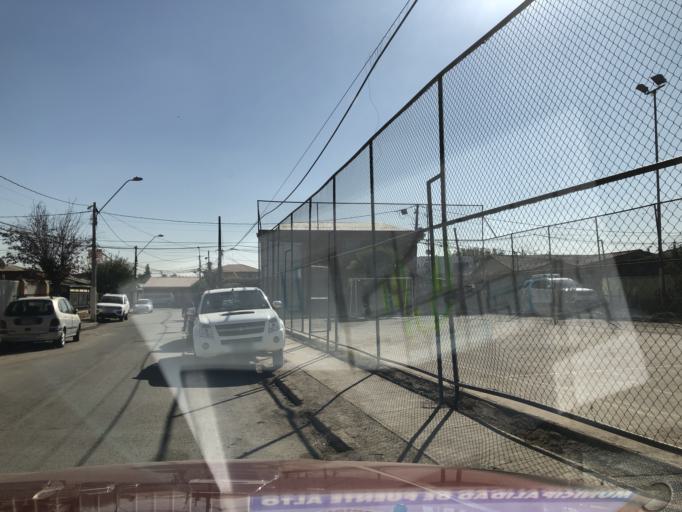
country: CL
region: Santiago Metropolitan
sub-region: Provincia de Cordillera
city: Puente Alto
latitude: -33.5740
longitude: -70.5733
